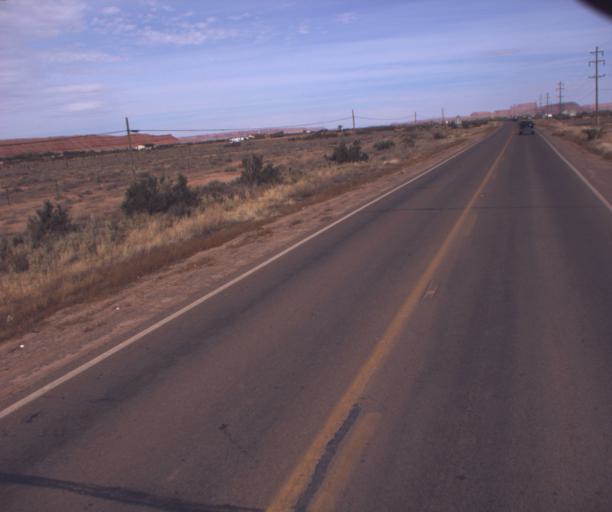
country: US
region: Arizona
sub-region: Apache County
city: Many Farms
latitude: 36.3571
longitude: -109.6162
